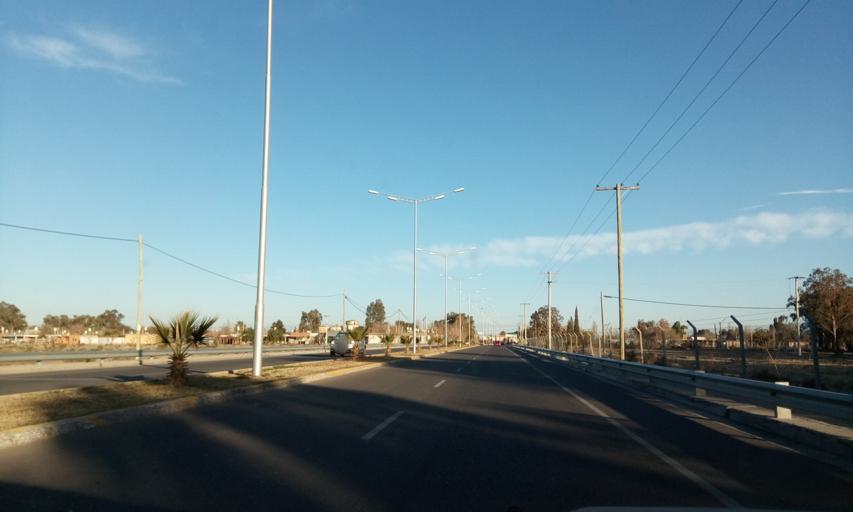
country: AR
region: San Juan
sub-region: Departamento de Rivadavia
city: Rivadavia
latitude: -31.5212
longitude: -68.6287
